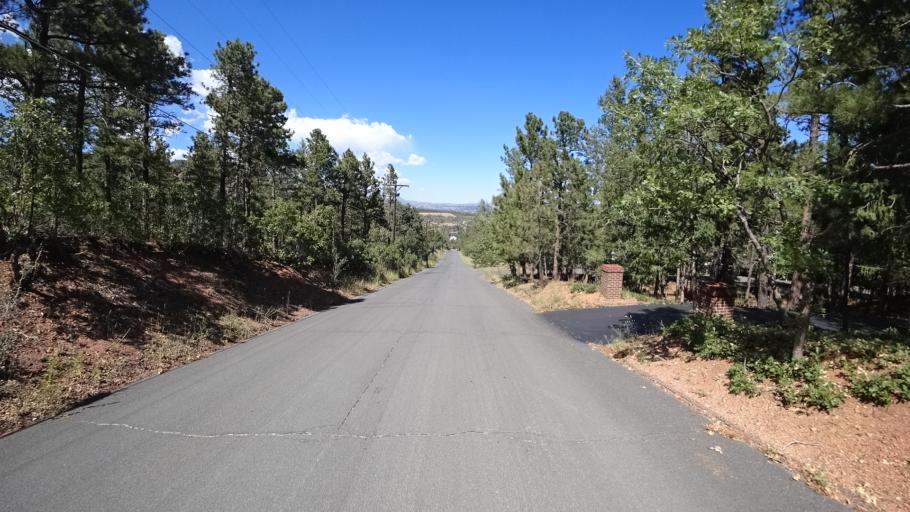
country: US
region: Colorado
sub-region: El Paso County
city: Colorado Springs
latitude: 38.7826
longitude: -104.8636
